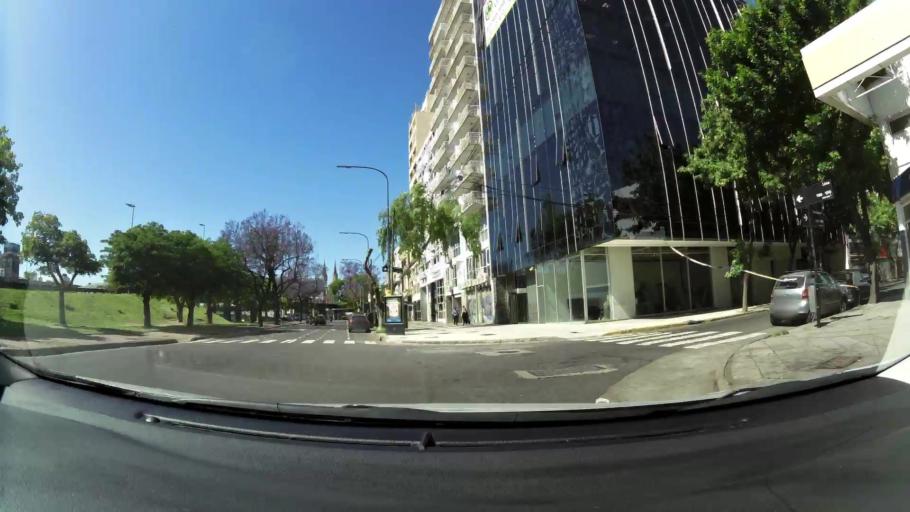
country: AR
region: Buenos Aires F.D.
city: Buenos Aires
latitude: -34.6209
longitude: -58.3815
